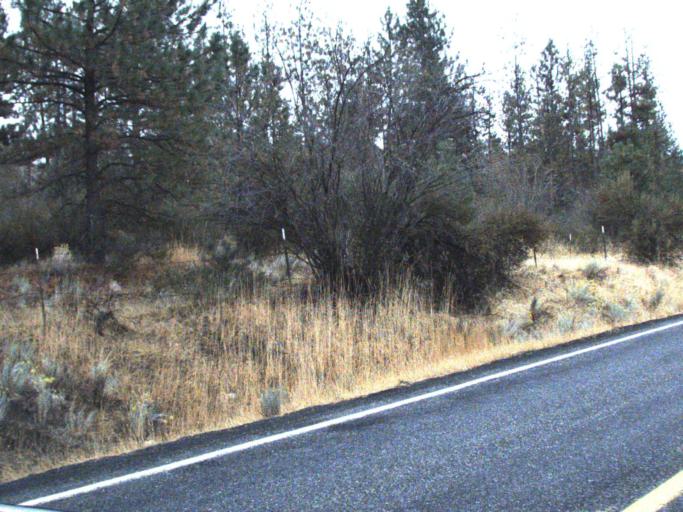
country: US
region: Washington
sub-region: Lincoln County
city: Davenport
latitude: 47.7954
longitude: -117.8910
